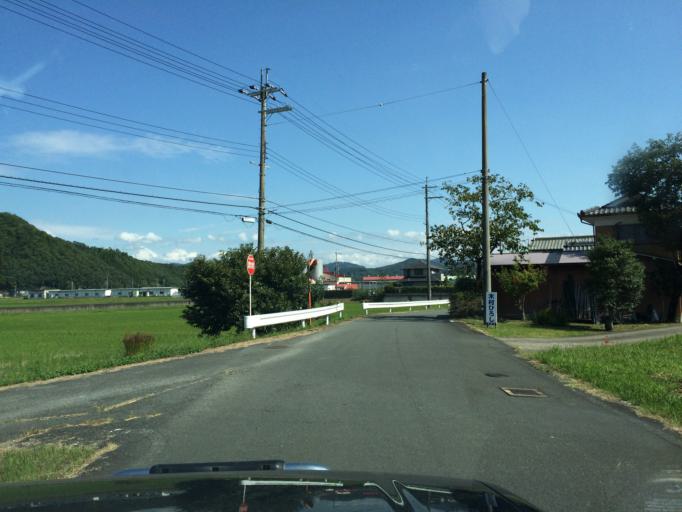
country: JP
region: Kyoto
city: Kameoka
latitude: 35.1064
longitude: 135.4471
